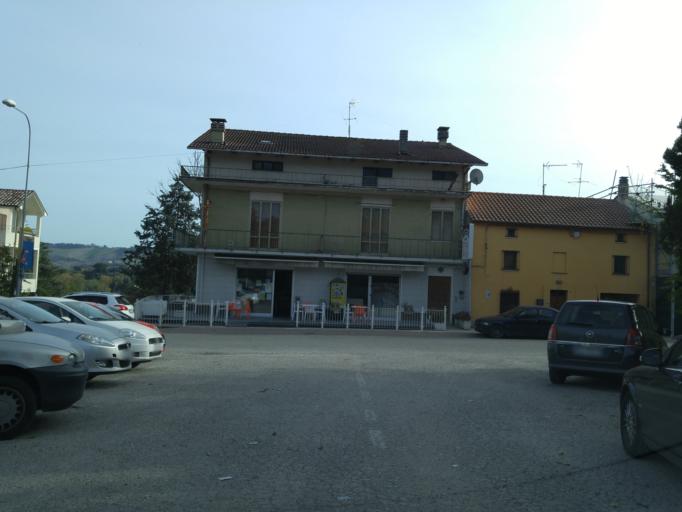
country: IT
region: The Marches
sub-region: Provincia di Pesaro e Urbino
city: Saltara
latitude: 43.7433
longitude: 12.9085
